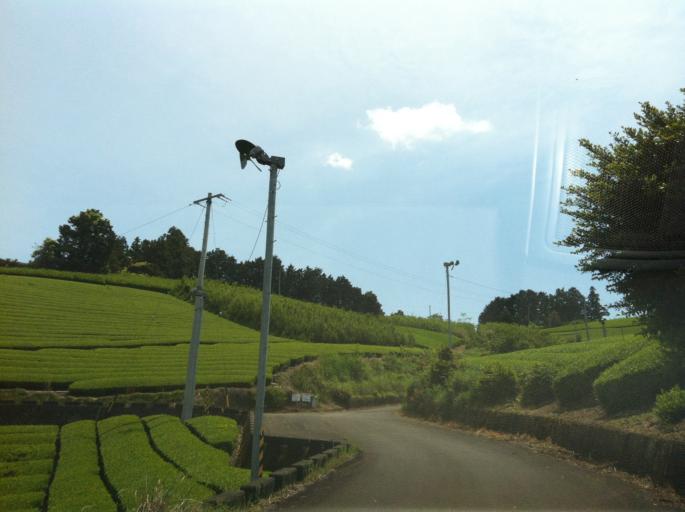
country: JP
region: Shizuoka
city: Shizuoka-shi
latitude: 35.0338
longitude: 138.4337
